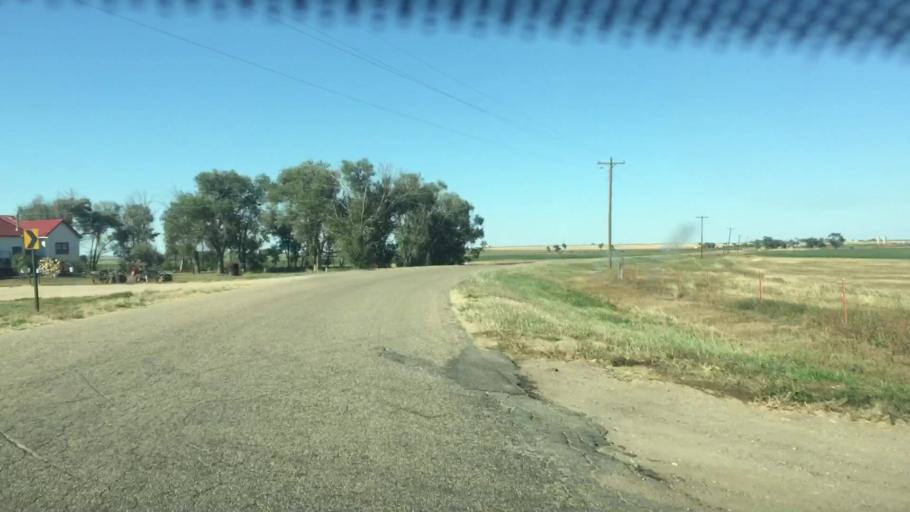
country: US
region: Colorado
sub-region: Prowers County
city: Lamar
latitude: 38.1005
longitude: -102.5212
